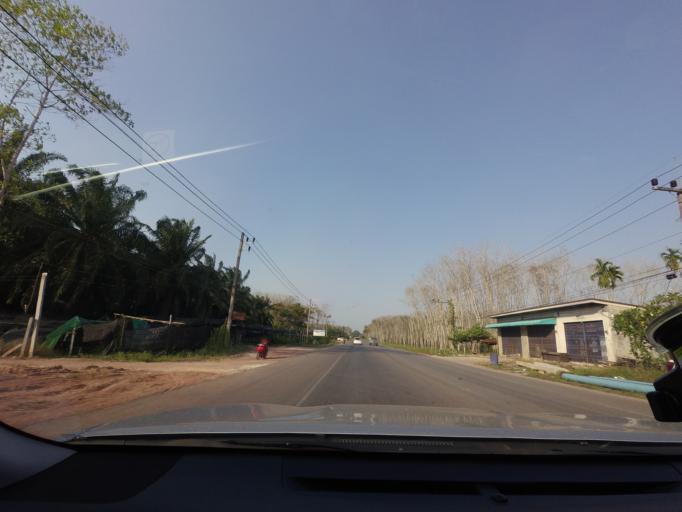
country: TH
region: Surat Thani
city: Phrasaeng
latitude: 8.5748
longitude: 99.2754
